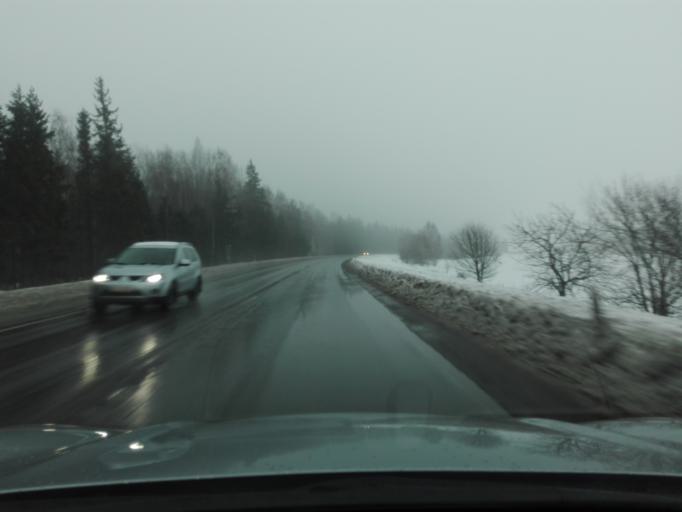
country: EE
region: Raplamaa
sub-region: Kohila vald
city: Kohila
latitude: 59.2294
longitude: 24.7757
